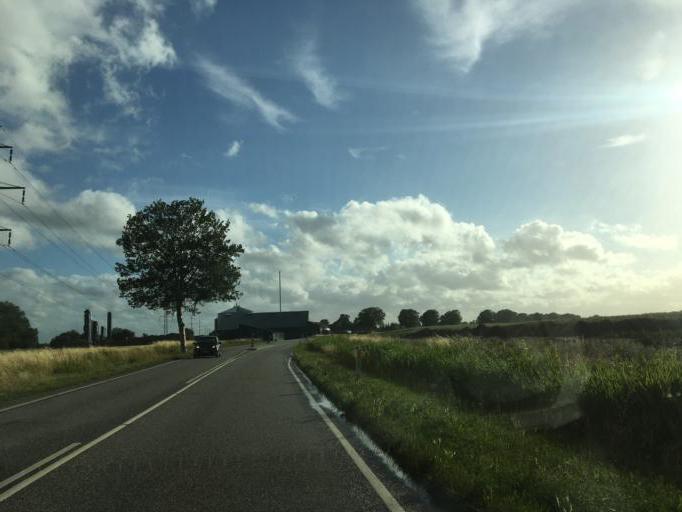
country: DK
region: Zealand
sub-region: Solrod Kommune
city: Solrod
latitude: 55.5172
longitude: 12.1785
